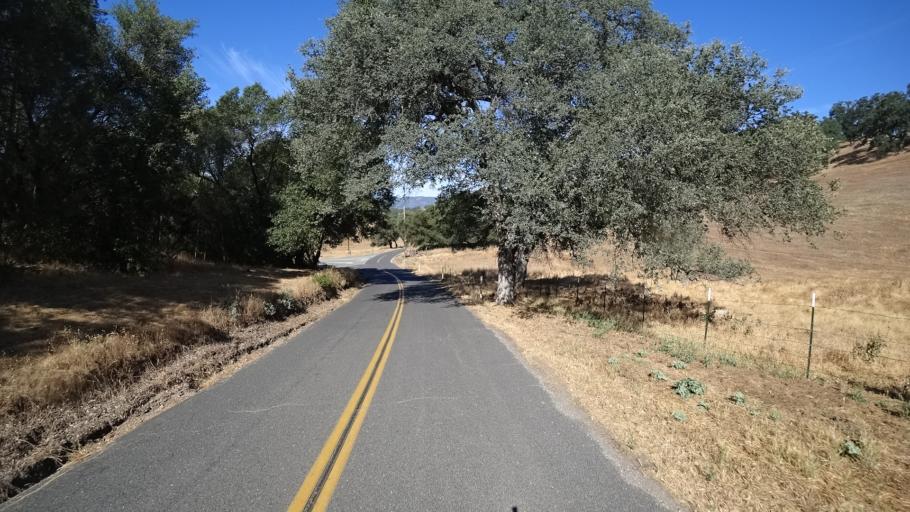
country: US
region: California
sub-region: Calaveras County
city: San Andreas
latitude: 38.1522
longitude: -120.5970
